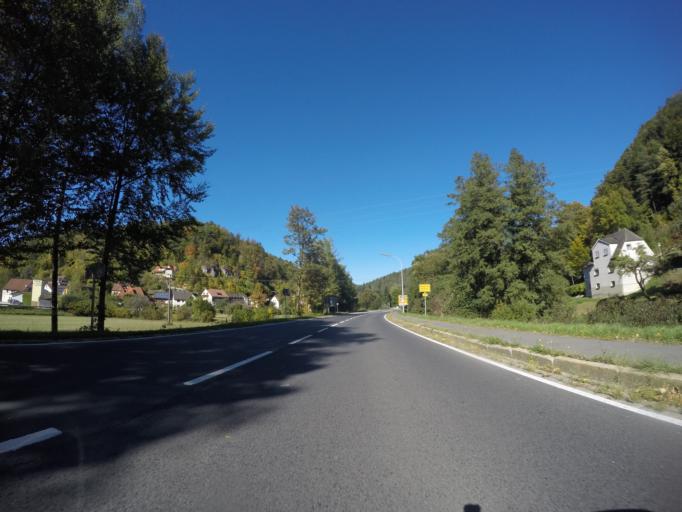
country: DE
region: Bavaria
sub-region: Upper Franconia
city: Gossweinstein
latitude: 49.7786
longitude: 11.3348
